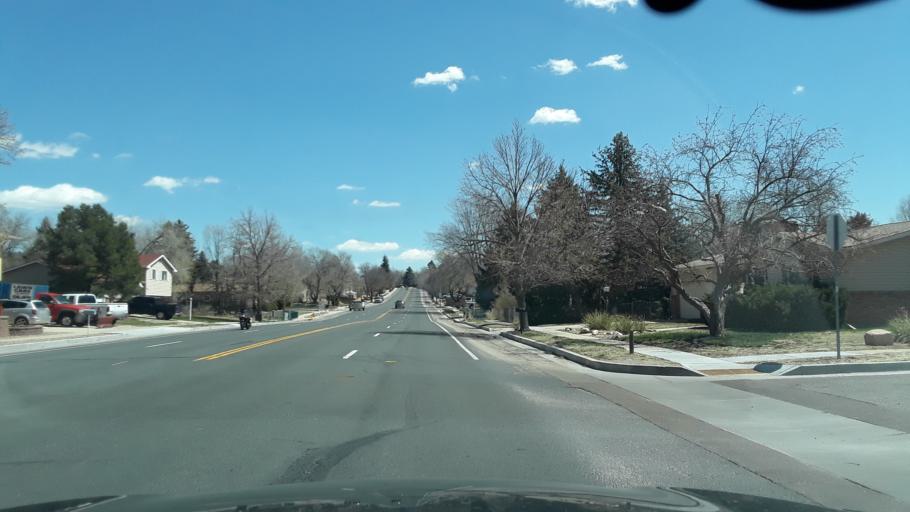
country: US
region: Colorado
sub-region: El Paso County
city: Cimarron Hills
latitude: 38.8542
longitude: -104.7377
